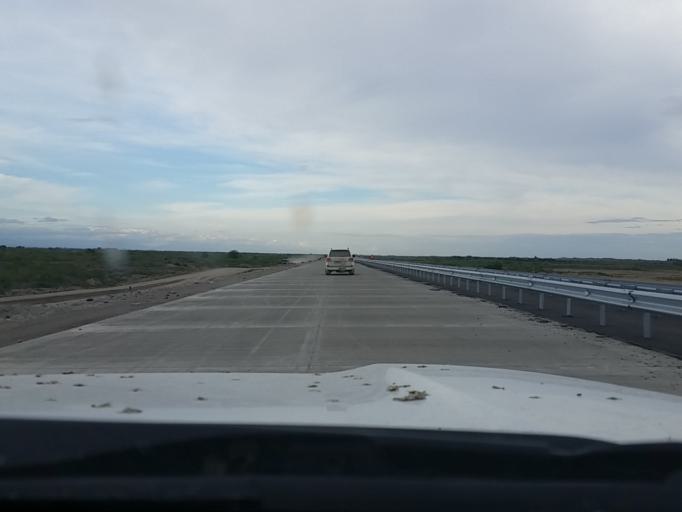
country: KZ
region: Almaty Oblysy
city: Zharkent
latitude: 44.1017
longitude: 80.0757
